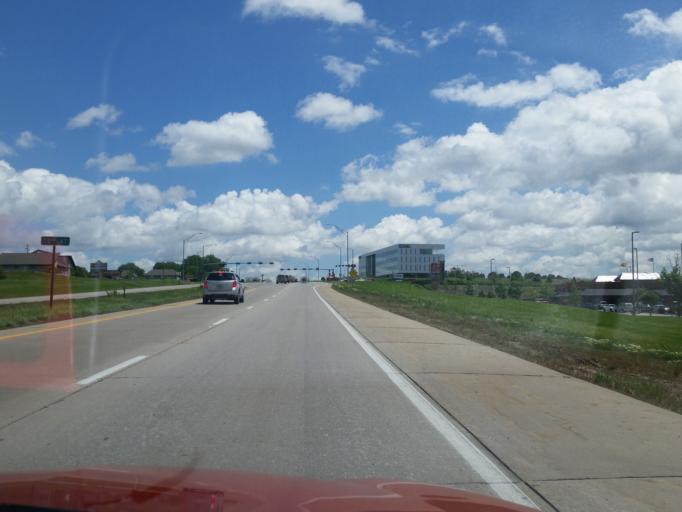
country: US
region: Nebraska
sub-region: Sarpy County
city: Papillion
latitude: 41.1381
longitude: -96.0270
